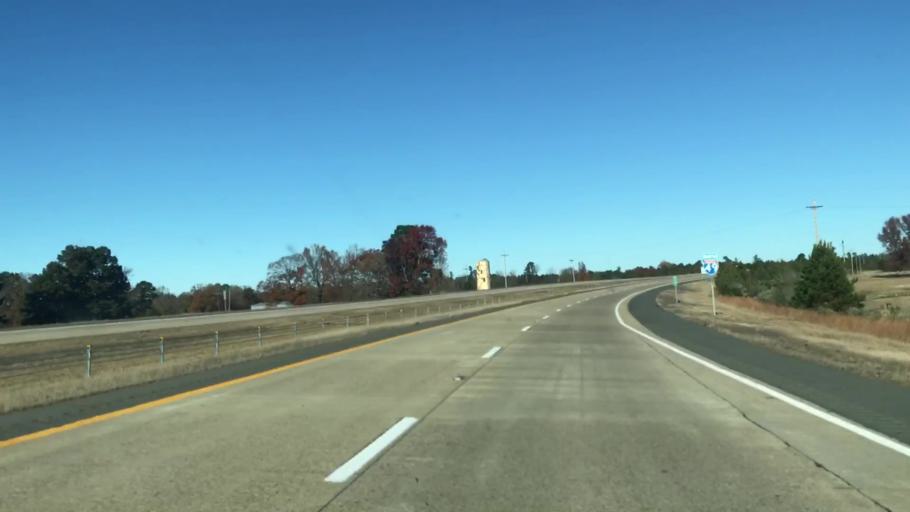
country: US
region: Texas
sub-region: Bowie County
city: Texarkana
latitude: 33.2530
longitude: -93.8920
